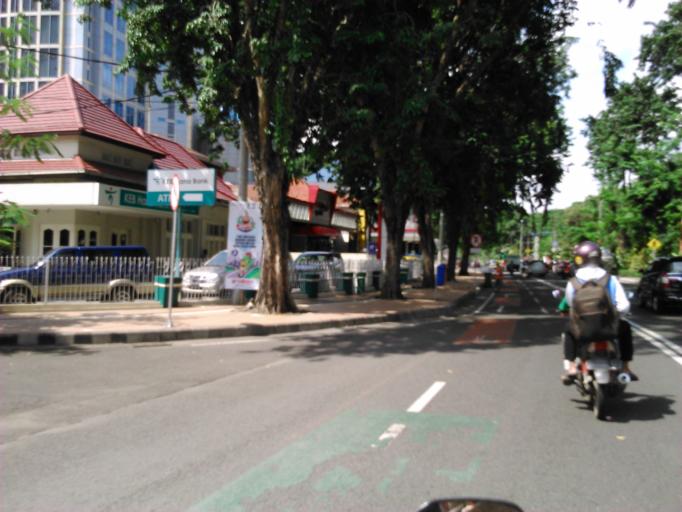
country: ID
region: East Java
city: Jagirsidosermo
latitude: -7.2898
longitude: 112.7391
